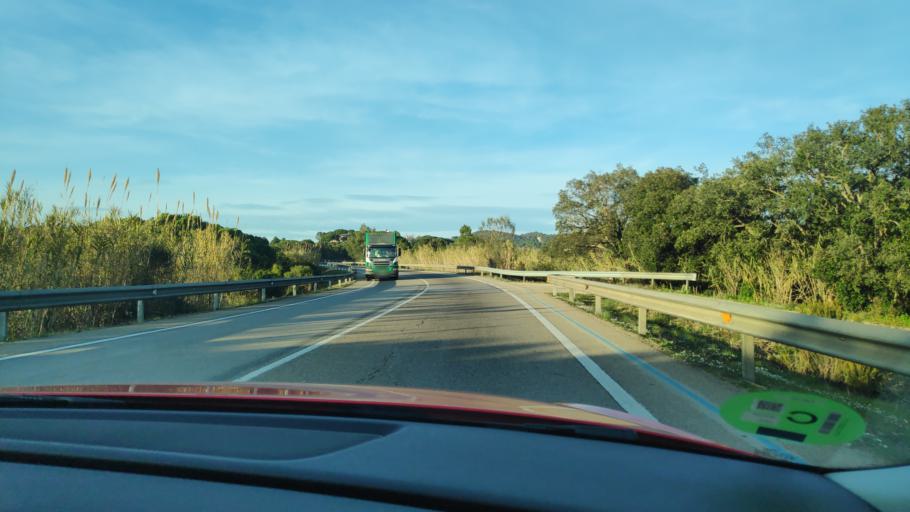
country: ES
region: Catalonia
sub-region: Provincia de Girona
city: Lloret de Mar
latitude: 41.7196
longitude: 2.8256
